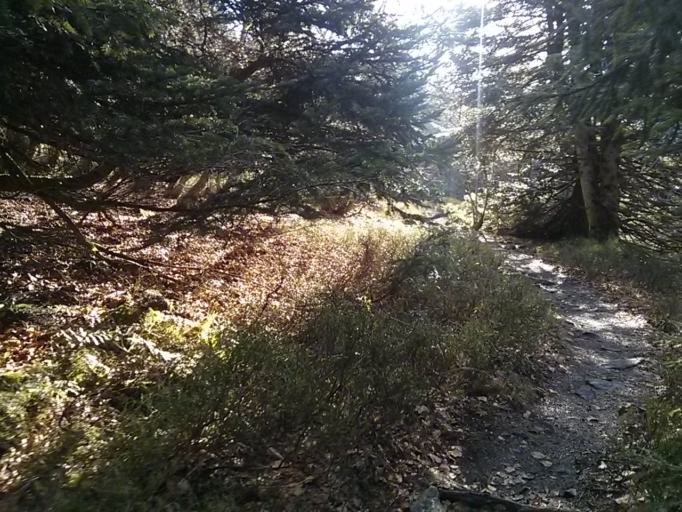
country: FR
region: Rhone-Alpes
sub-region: Departement de la Loire
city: Saint-Julien-Molin-Molette
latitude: 45.3815
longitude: 4.5777
